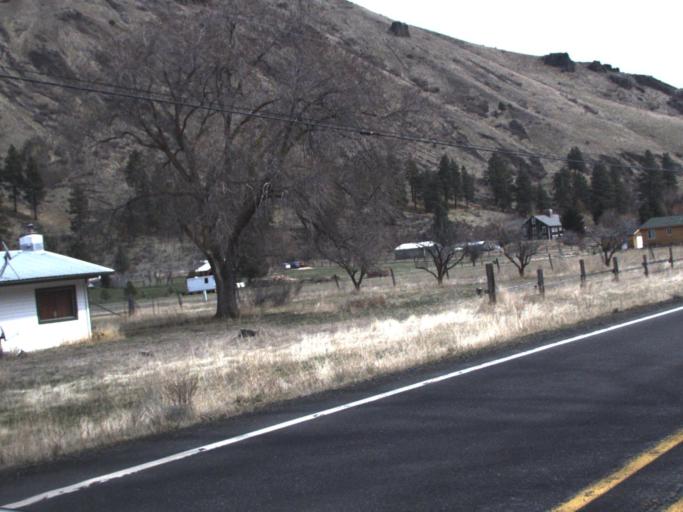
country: US
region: Washington
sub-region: Yakima County
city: Tieton
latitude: 46.8065
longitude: -120.9150
